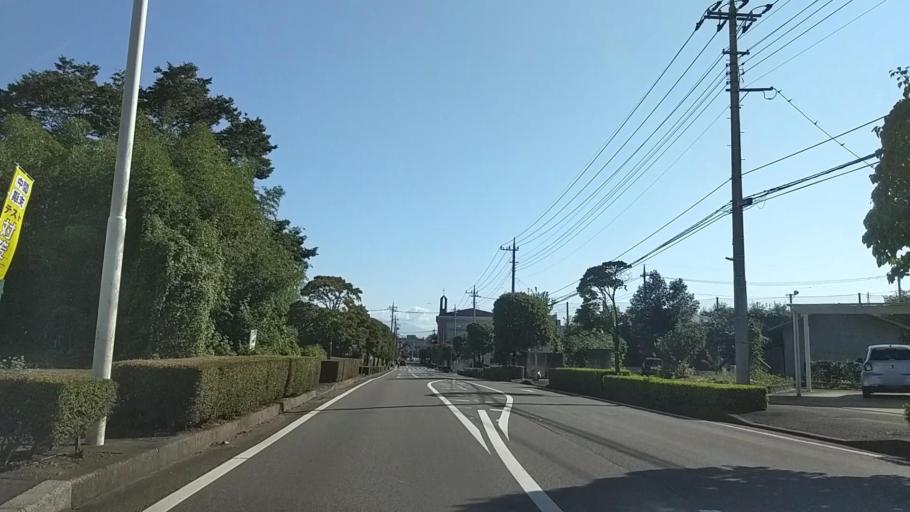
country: JP
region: Gunma
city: Annaka
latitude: 36.3249
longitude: 138.8983
